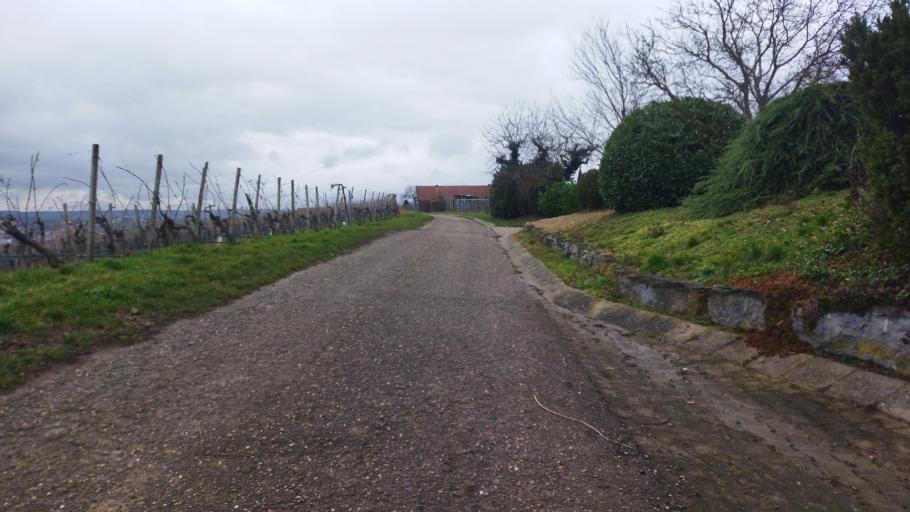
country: DE
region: Baden-Wuerttemberg
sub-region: Regierungsbezirk Stuttgart
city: Talheim
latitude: 49.0709
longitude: 9.1765
